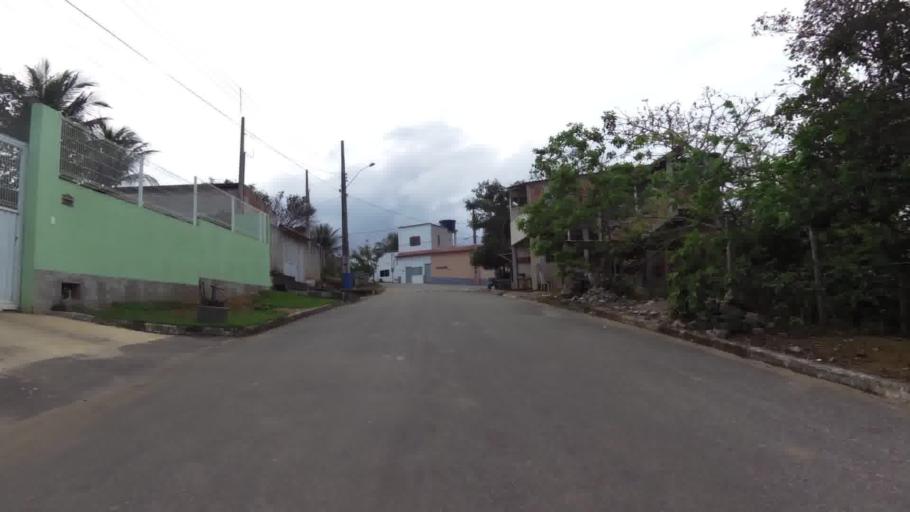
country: BR
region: Espirito Santo
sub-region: Piuma
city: Piuma
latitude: -20.7925
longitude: -40.6404
